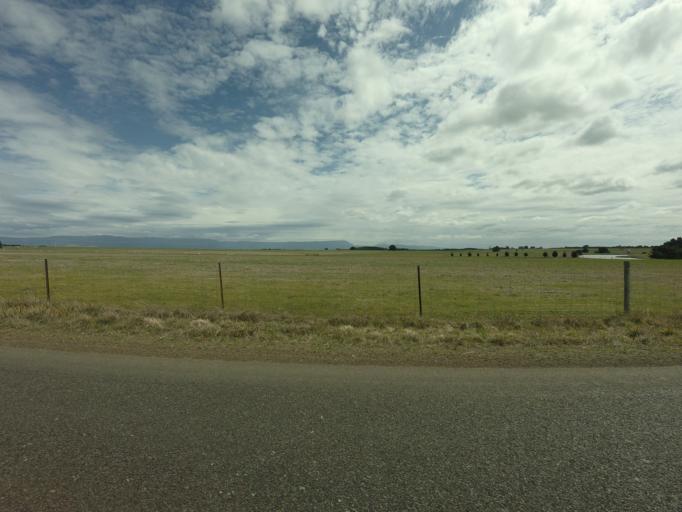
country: AU
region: Tasmania
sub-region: Northern Midlands
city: Longford
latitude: -41.6992
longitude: 147.1965
